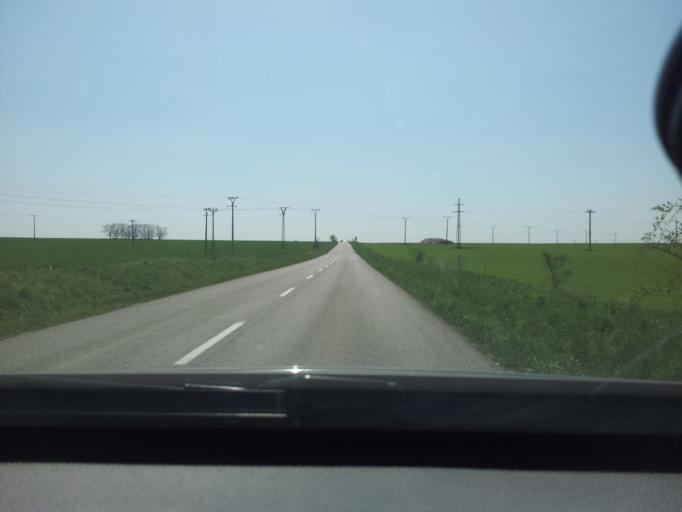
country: SK
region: Nitriansky
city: Zlate Moravce
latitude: 48.3724
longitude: 18.4058
